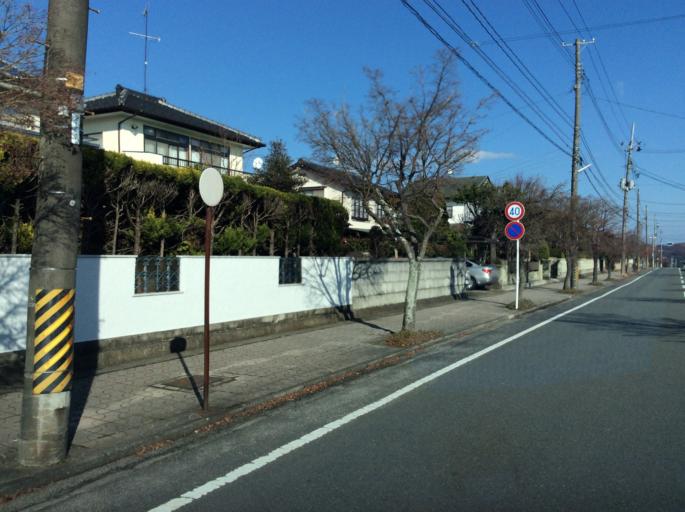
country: JP
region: Fukushima
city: Iwaki
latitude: 37.0268
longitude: 140.9112
